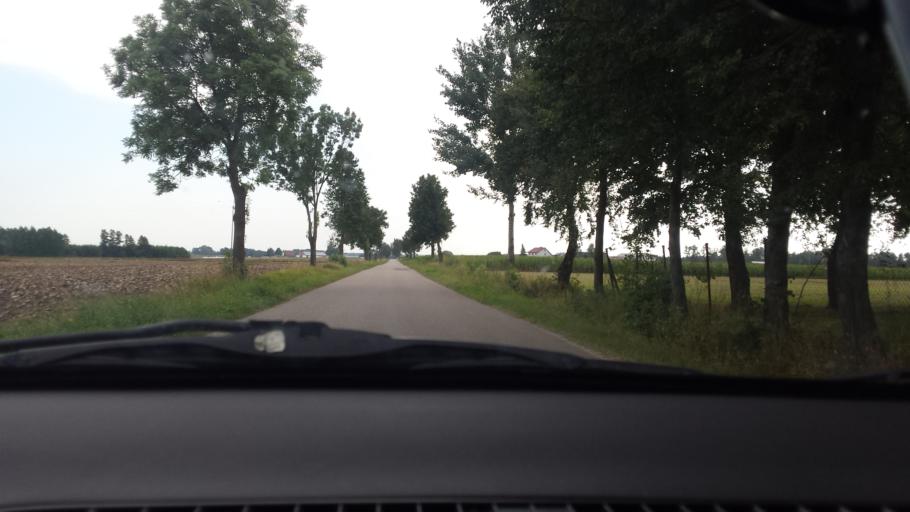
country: PL
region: Masovian Voivodeship
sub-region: Powiat makowski
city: Sypniewo
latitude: 52.9863
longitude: 21.3554
